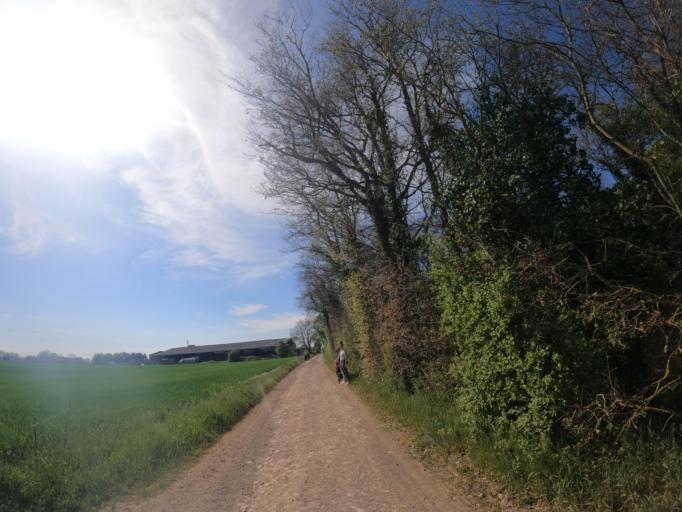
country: FR
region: Poitou-Charentes
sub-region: Departement des Deux-Sevres
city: Saint-Varent
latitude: 46.9143
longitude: -0.2131
